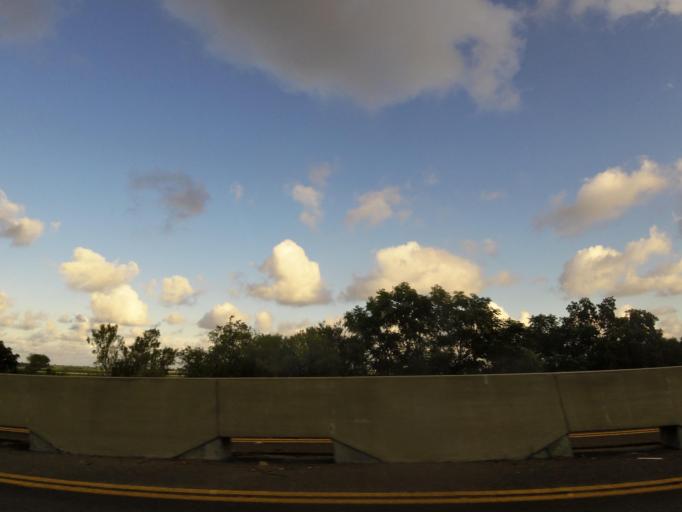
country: US
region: Georgia
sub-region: Glynn County
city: Saint Simon Mills
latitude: 31.1661
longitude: -81.4426
